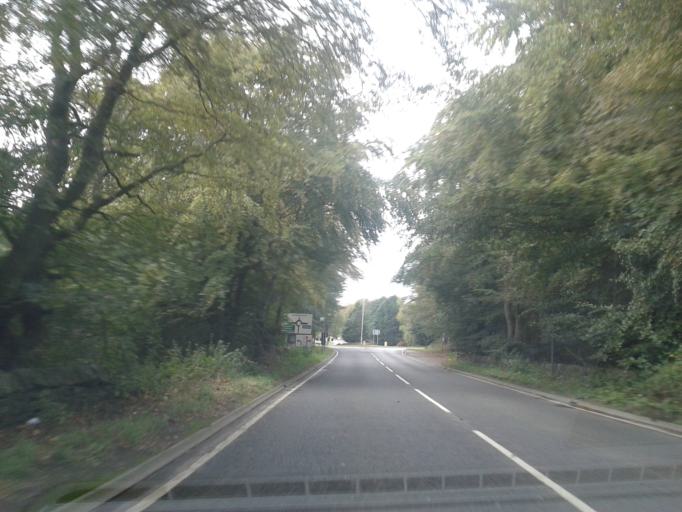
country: GB
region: Scotland
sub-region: Fife
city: Ladybank
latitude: 56.3014
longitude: -3.1223
